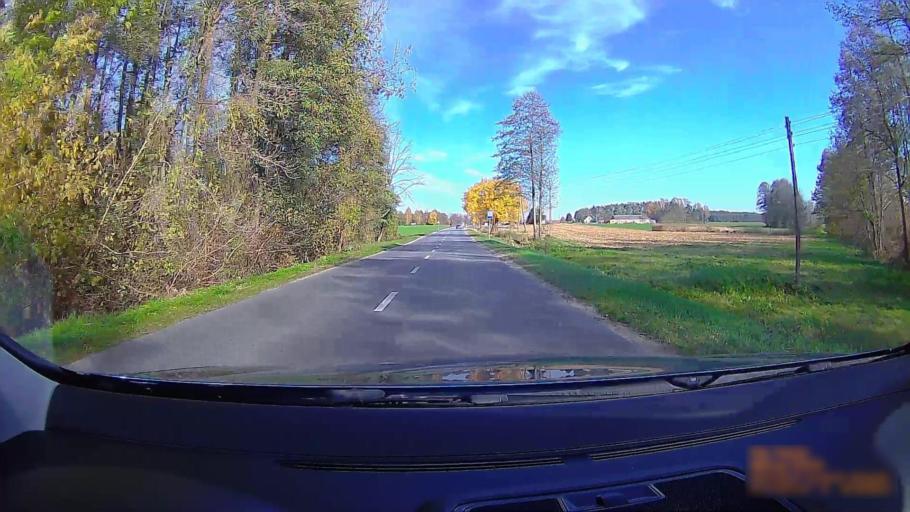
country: PL
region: Greater Poland Voivodeship
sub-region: Powiat ostrzeszowski
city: Doruchow
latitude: 51.3866
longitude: 18.0492
